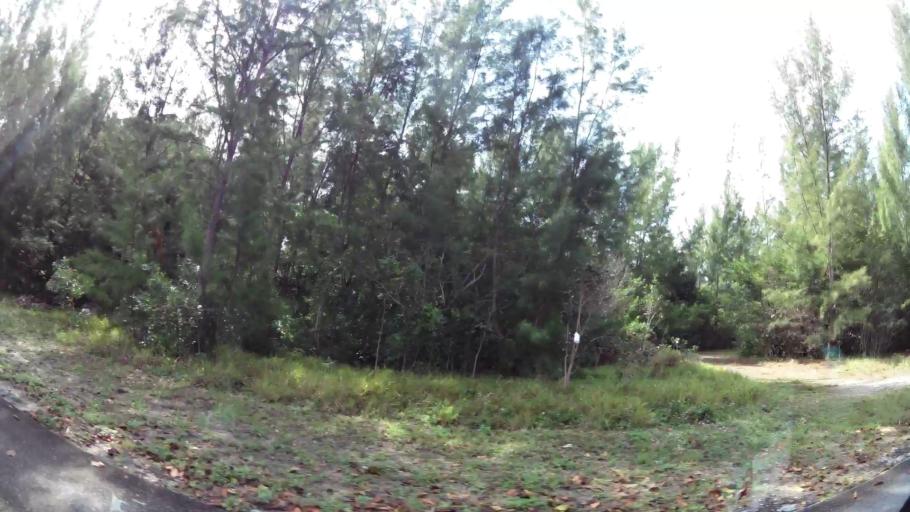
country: BS
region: Freeport
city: Lucaya
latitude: 26.5536
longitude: -78.5466
